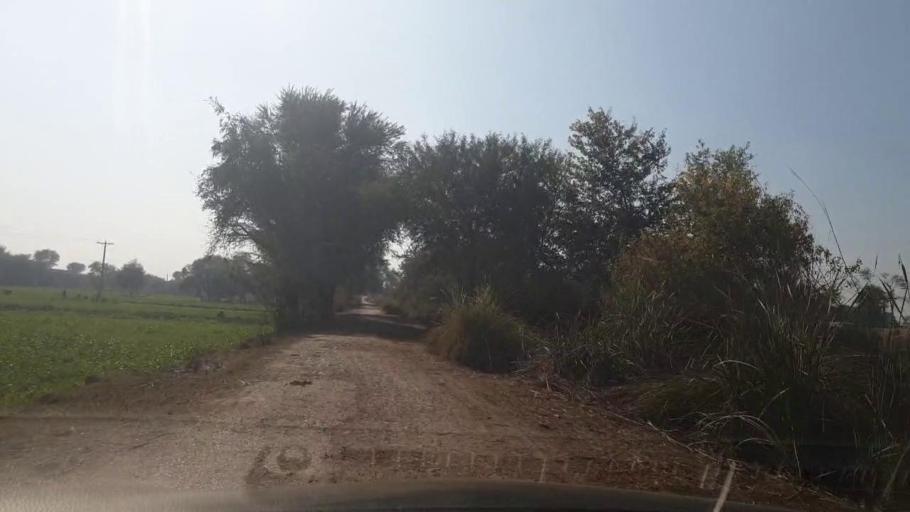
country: PK
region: Sindh
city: Ubauro
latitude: 28.1391
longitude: 69.6843
